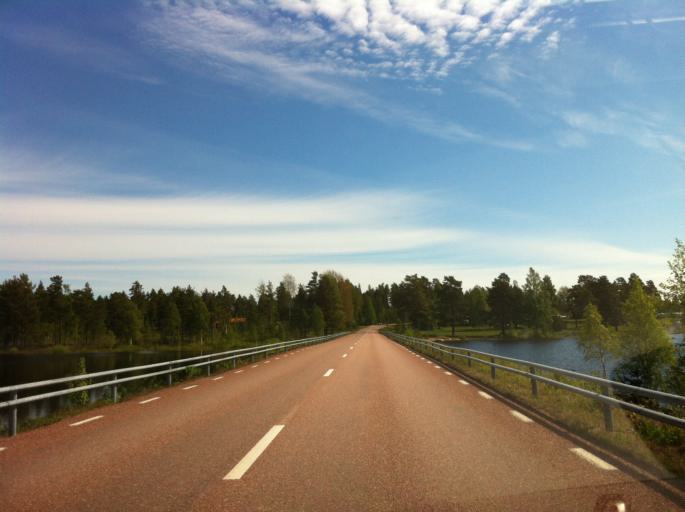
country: SE
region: Dalarna
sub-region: Mora Kommun
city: Mora
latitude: 60.8992
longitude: 14.5733
